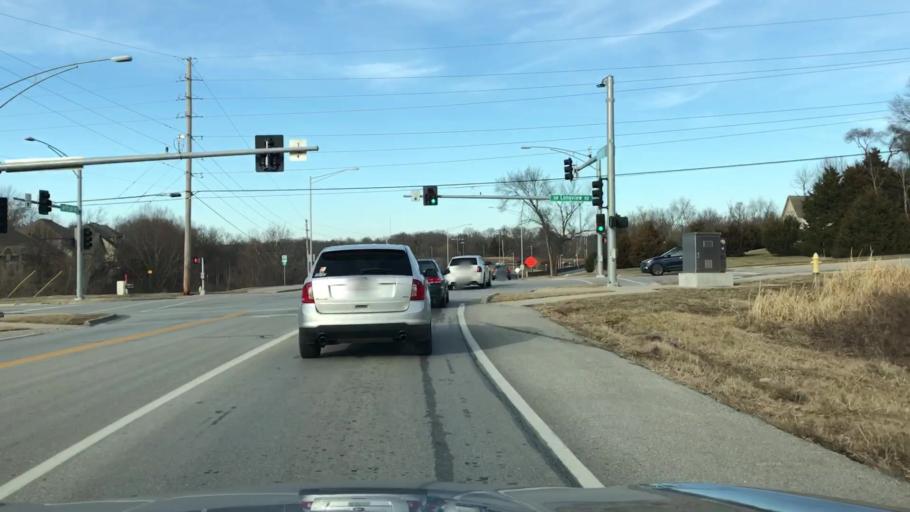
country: US
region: Missouri
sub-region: Jackson County
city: Lees Summit
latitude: 38.9042
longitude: -94.4148
